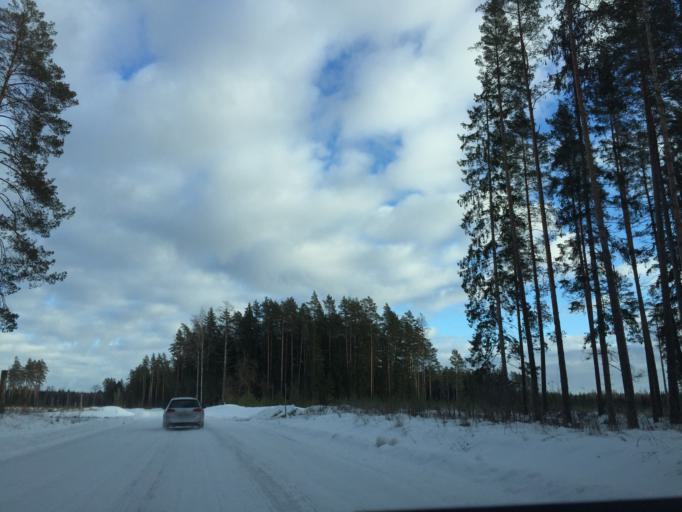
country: LV
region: Ogre
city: Jumprava
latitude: 56.5485
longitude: 24.8760
